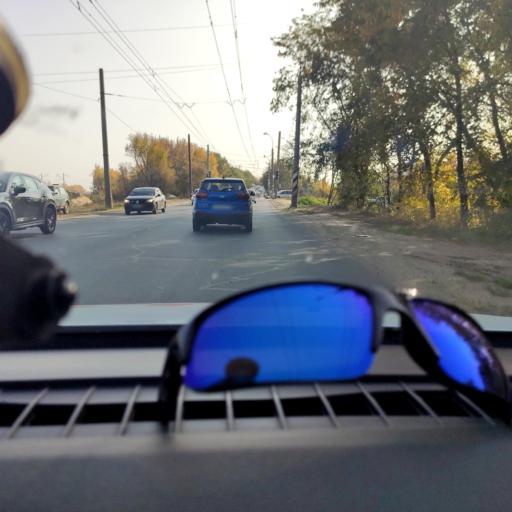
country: RU
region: Samara
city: Samara
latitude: 53.1544
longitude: 50.0921
